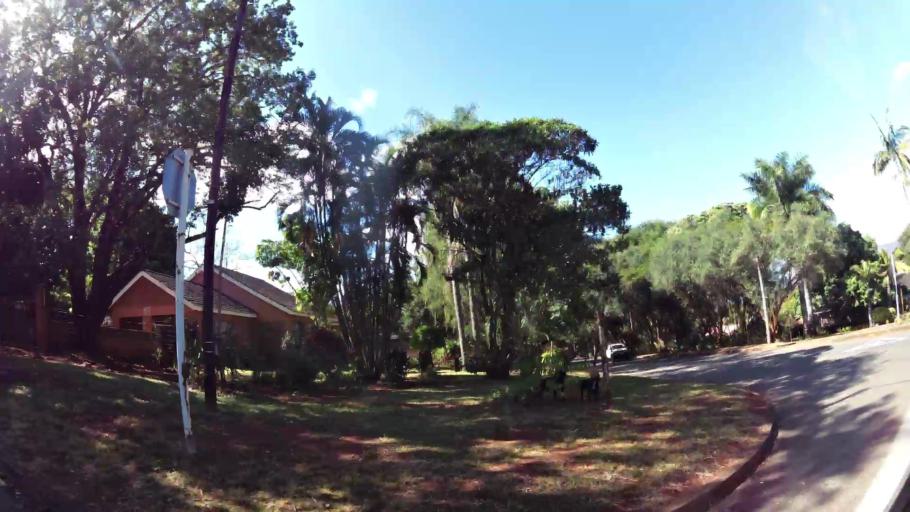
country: ZA
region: Limpopo
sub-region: Mopani District Municipality
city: Tzaneen
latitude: -23.8133
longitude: 30.1500
